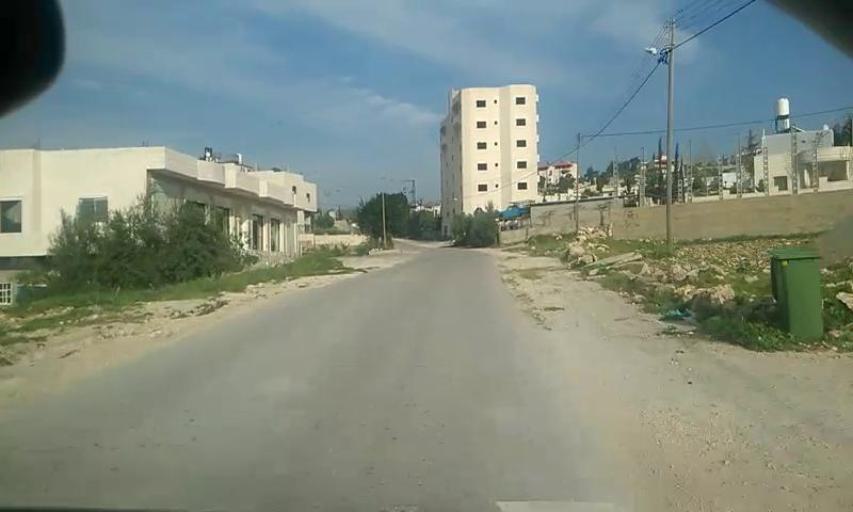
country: PS
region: West Bank
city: Nuba
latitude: 31.6141
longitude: 35.0276
